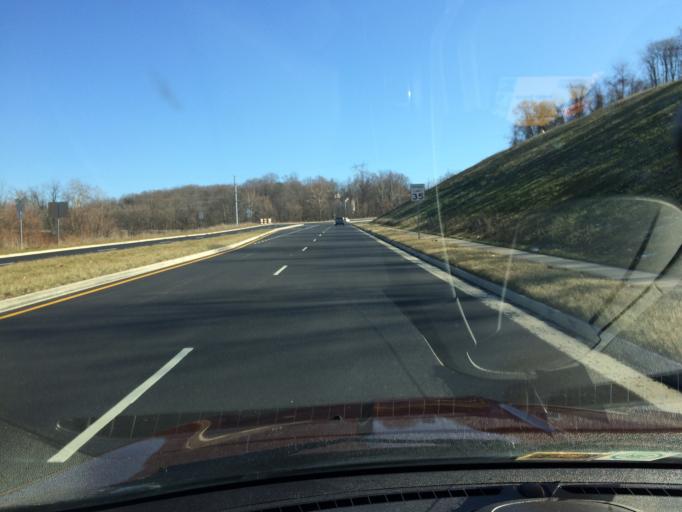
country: US
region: Virginia
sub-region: Botetourt County
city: Daleville
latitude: 37.3900
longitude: -79.8991
